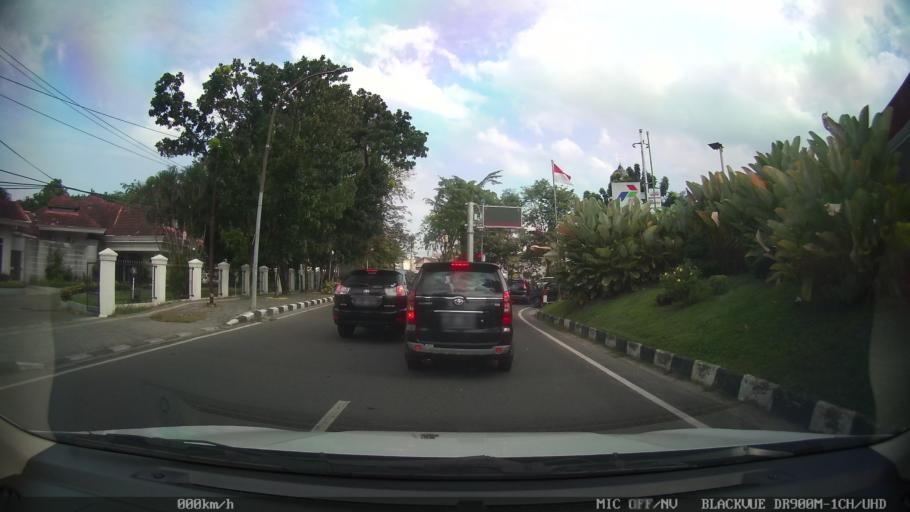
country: ID
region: North Sumatra
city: Medan
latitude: 3.5784
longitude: 98.6771
